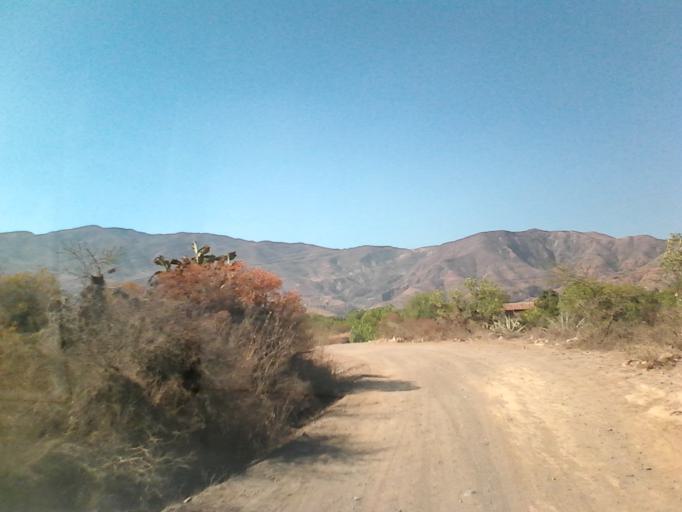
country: CO
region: Boyaca
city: Sachica
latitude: 5.5760
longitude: -73.5421
